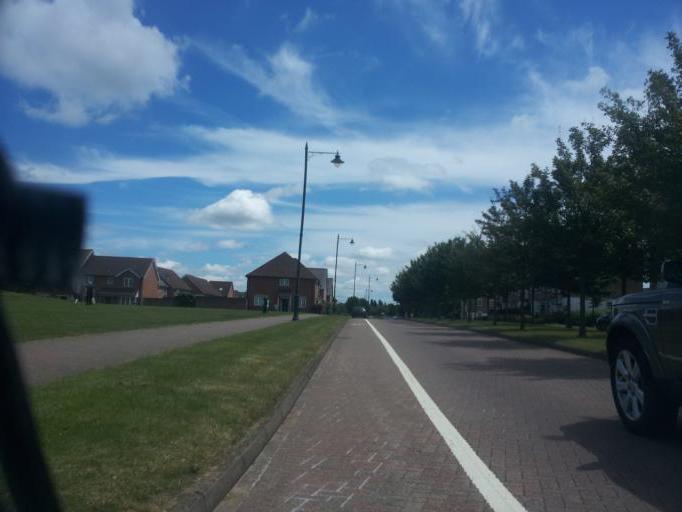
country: GB
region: England
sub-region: Kent
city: Kings Hill
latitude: 51.2725
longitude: 0.4055
